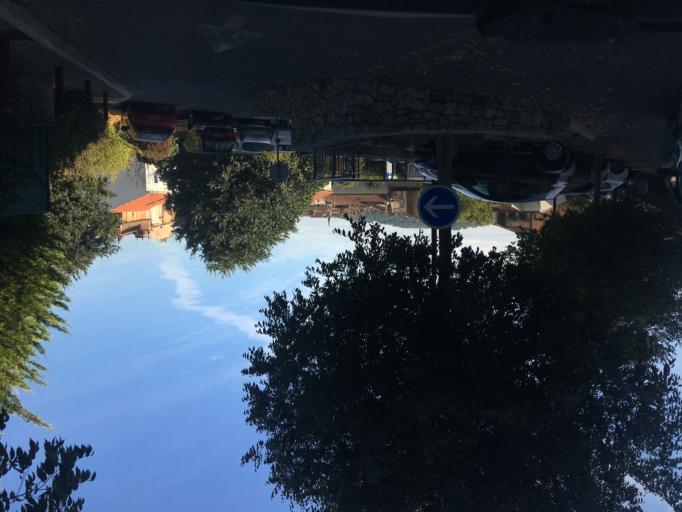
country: FR
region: Provence-Alpes-Cote d'Azur
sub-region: Departement du Var
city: Draguignan
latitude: 43.5399
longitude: 6.4688
